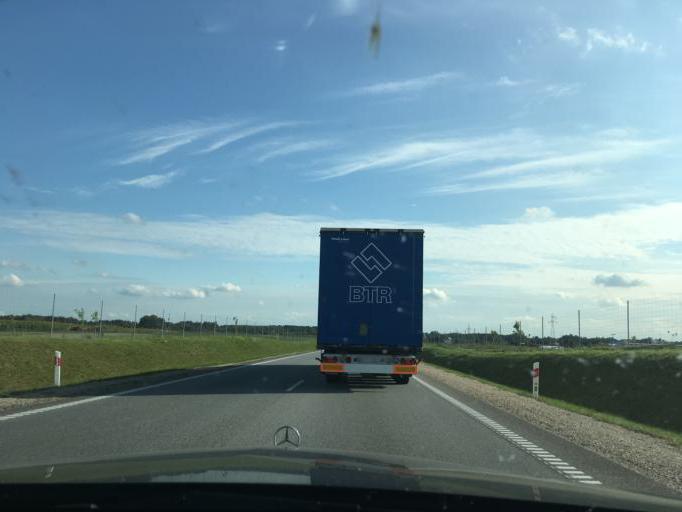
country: PL
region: Podlasie
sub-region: Powiat augustowski
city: Augustow
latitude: 53.8872
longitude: 22.8703
